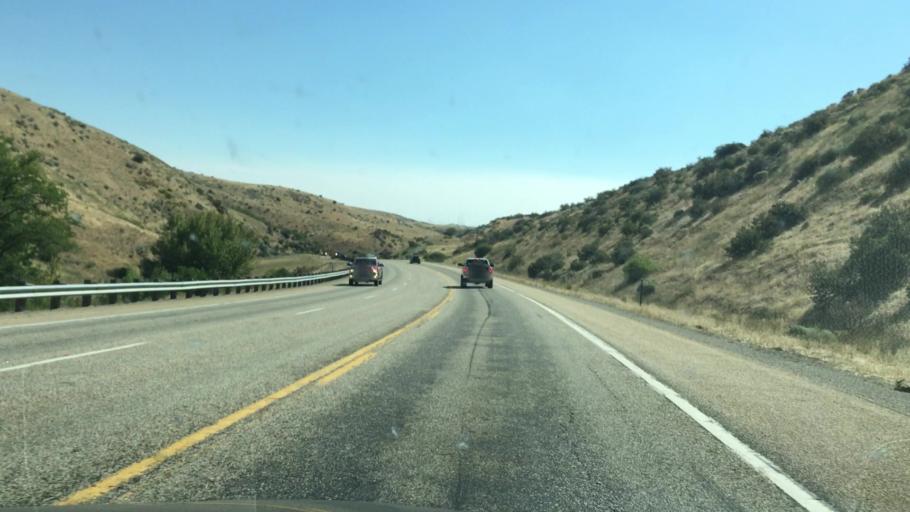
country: US
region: Idaho
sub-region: Ada County
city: Eagle
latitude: 43.8236
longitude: -116.2556
